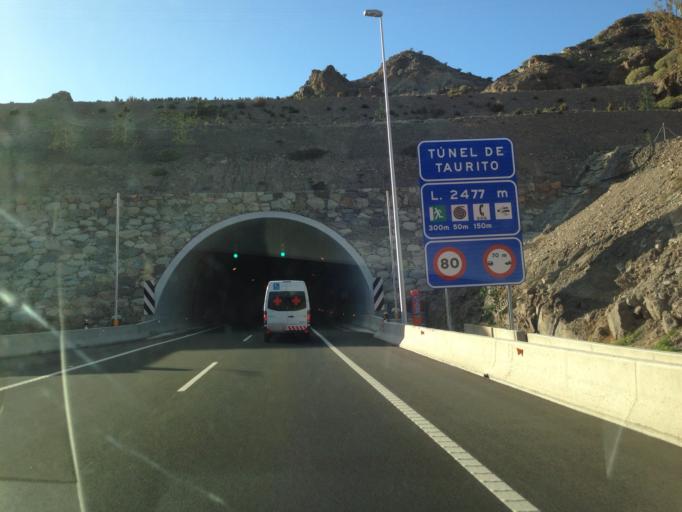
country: ES
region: Canary Islands
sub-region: Provincia de Las Palmas
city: Puerto Rico
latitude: 27.8101
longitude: -15.7267
